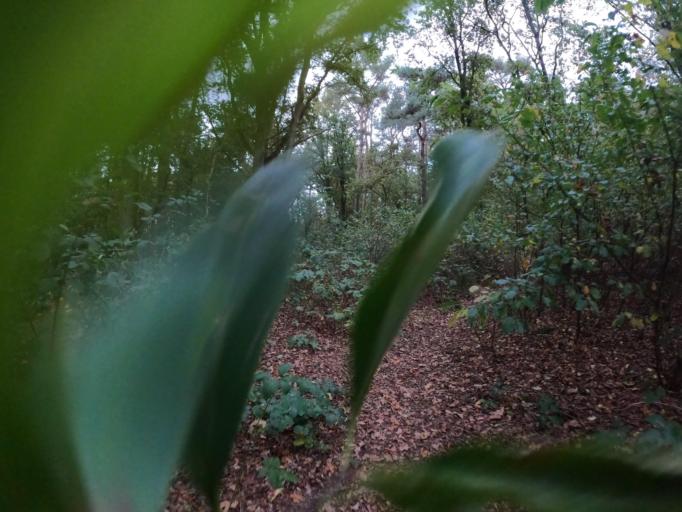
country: BE
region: Flanders
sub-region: Provincie Antwerpen
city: Nijlen
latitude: 51.1501
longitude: 4.6832
